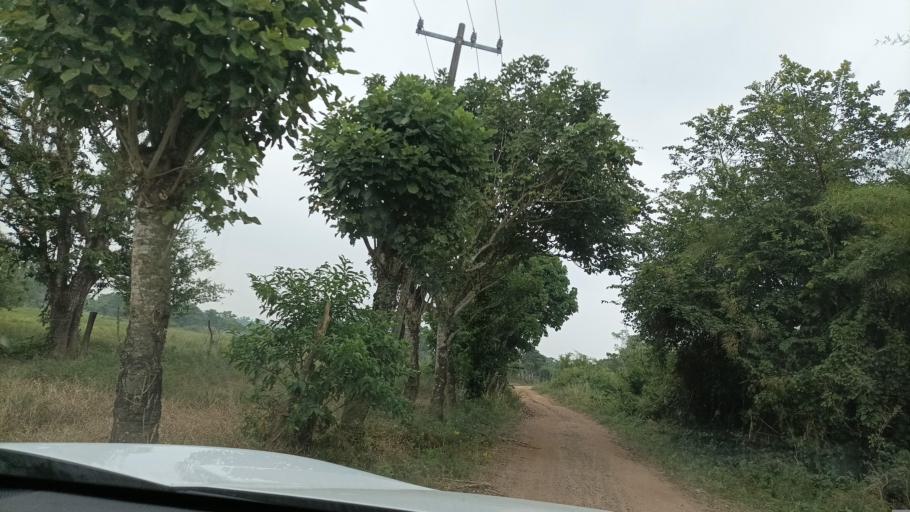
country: MX
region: Veracruz
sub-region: Uxpanapa
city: Poblado 10
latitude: 17.5575
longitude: -94.2263
